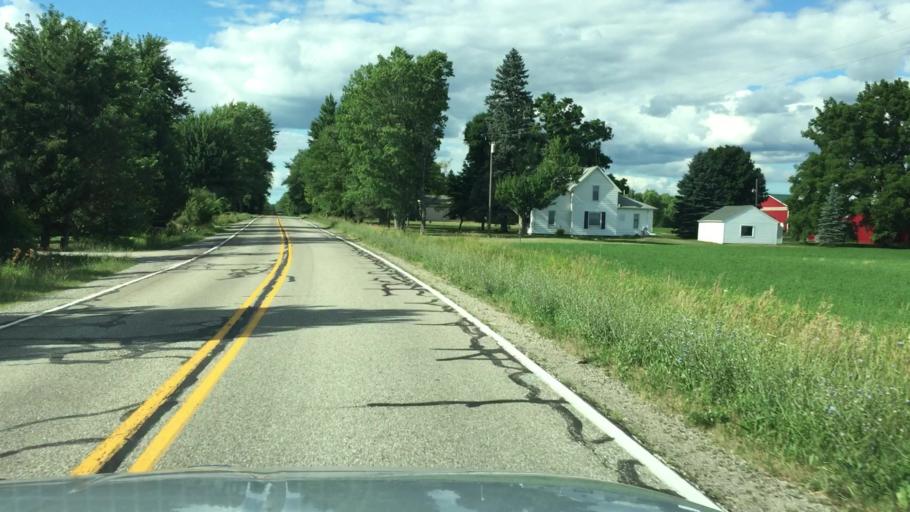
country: US
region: Michigan
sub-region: Saint Clair County
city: Capac
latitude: 43.0929
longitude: -82.9092
